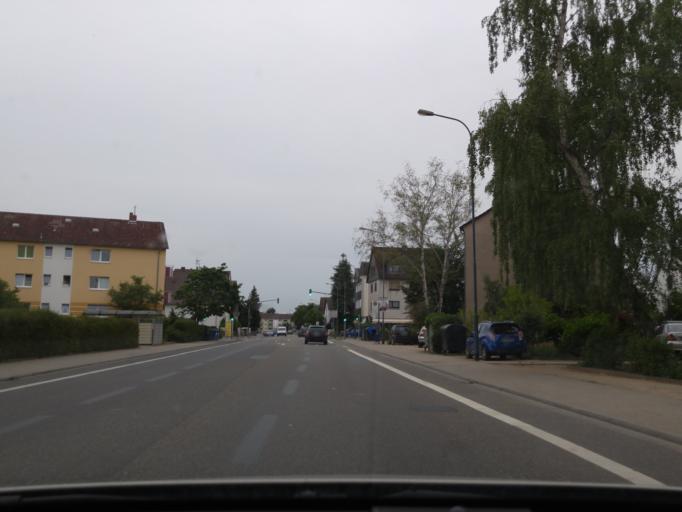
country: DE
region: Hesse
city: Langen
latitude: 49.9885
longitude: 8.6631
